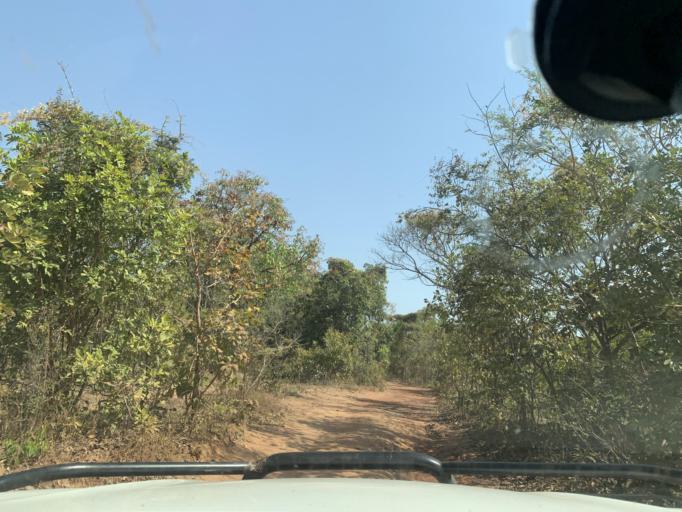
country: ML
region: Sikasso
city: Kolondieba
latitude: 10.8942
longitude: -6.7467
